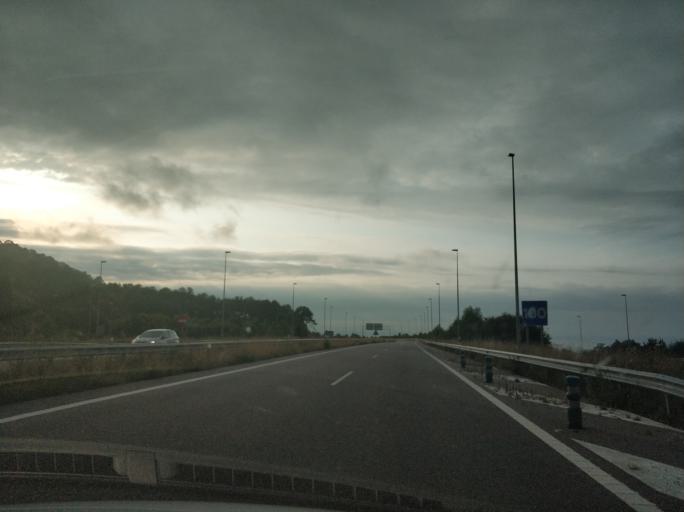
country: ES
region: Asturias
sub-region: Province of Asturias
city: Cudillero
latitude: 43.5536
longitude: -6.1690
